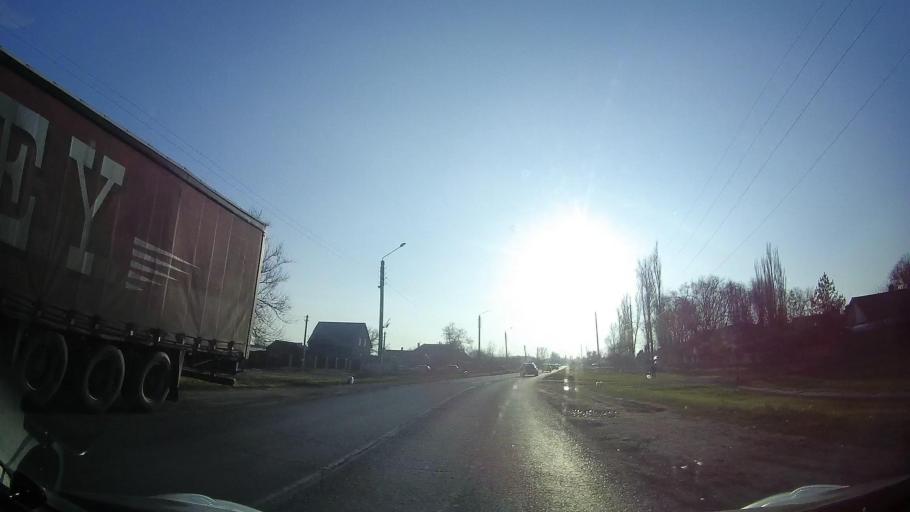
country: RU
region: Rostov
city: Ol'ginskaya
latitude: 47.1798
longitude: 39.9580
